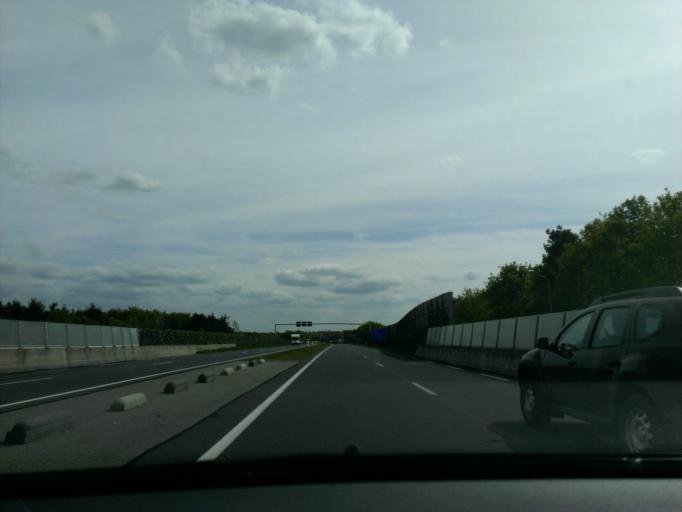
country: NL
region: Gelderland
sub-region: Gemeente Harderwijk
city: Harderwijk
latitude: 52.3416
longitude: 5.6448
